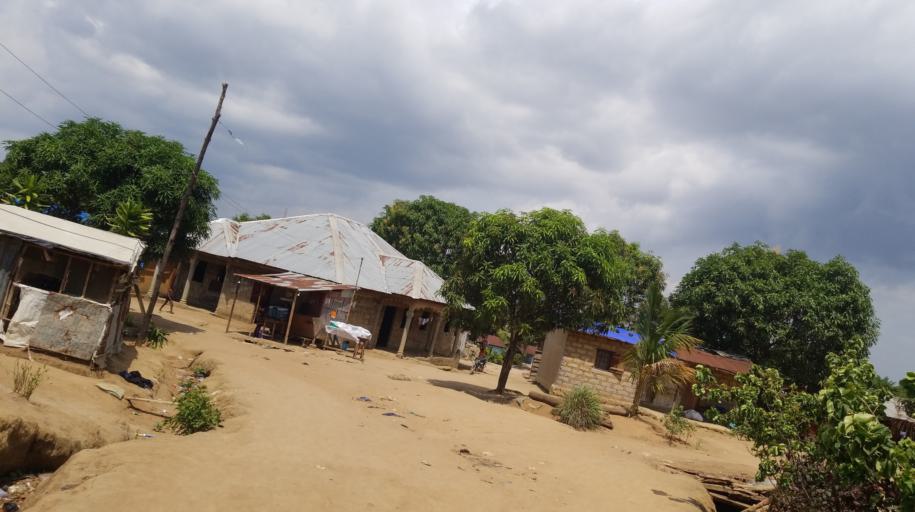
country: SL
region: Western Area
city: Waterloo
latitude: 8.3196
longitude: -13.0533
